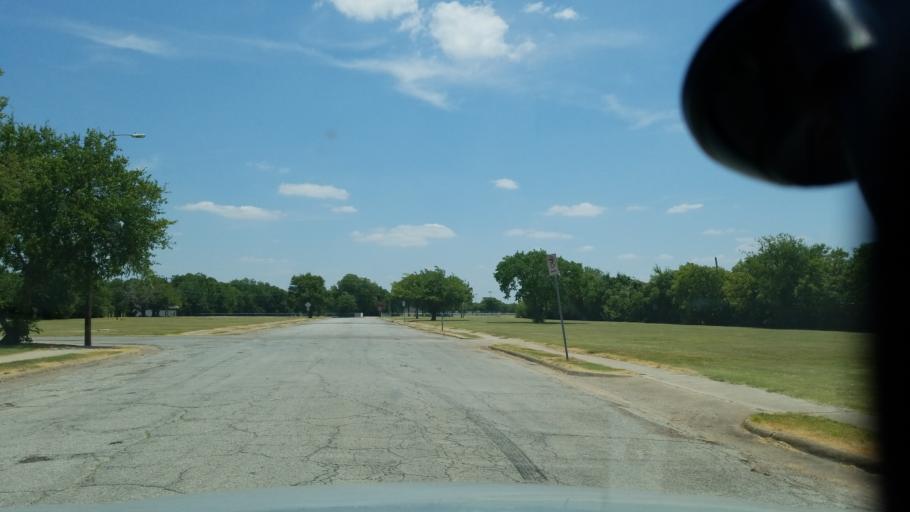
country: US
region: Texas
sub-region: Dallas County
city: Grand Prairie
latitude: 32.7525
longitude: -96.9730
